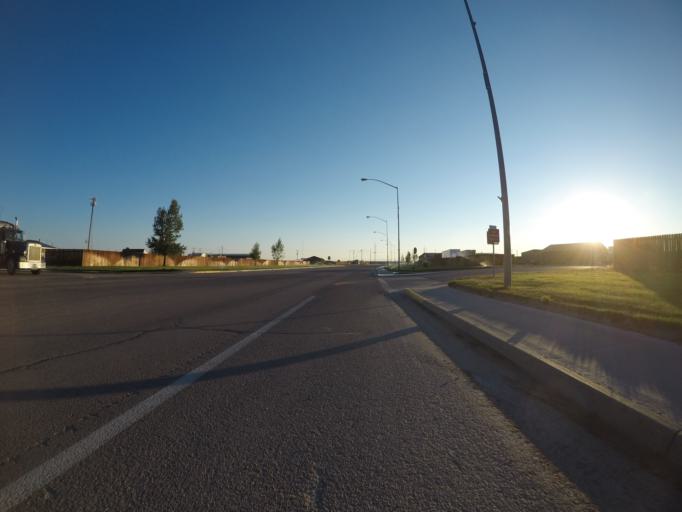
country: US
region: Wyoming
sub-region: Sublette County
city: Marbleton
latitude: 42.5574
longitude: -110.1087
